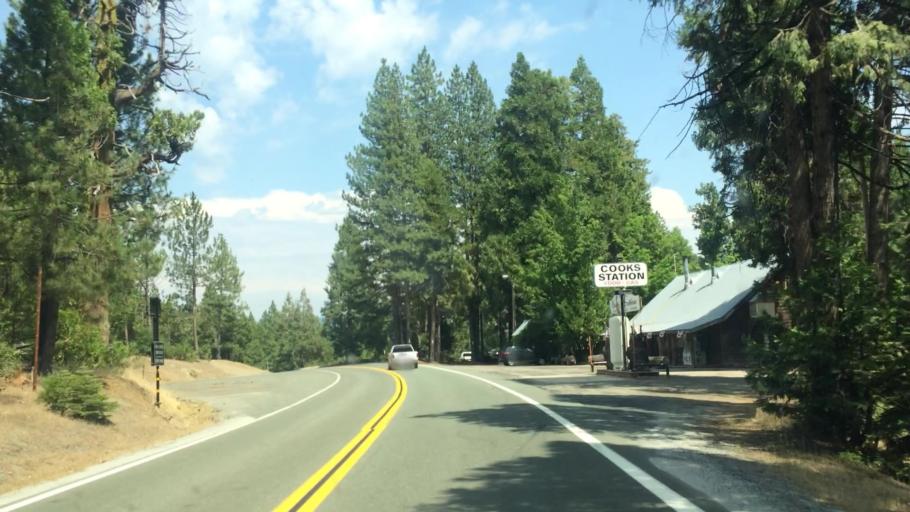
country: US
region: California
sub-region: Amador County
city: Pioneer
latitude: 38.5267
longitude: -120.4342
